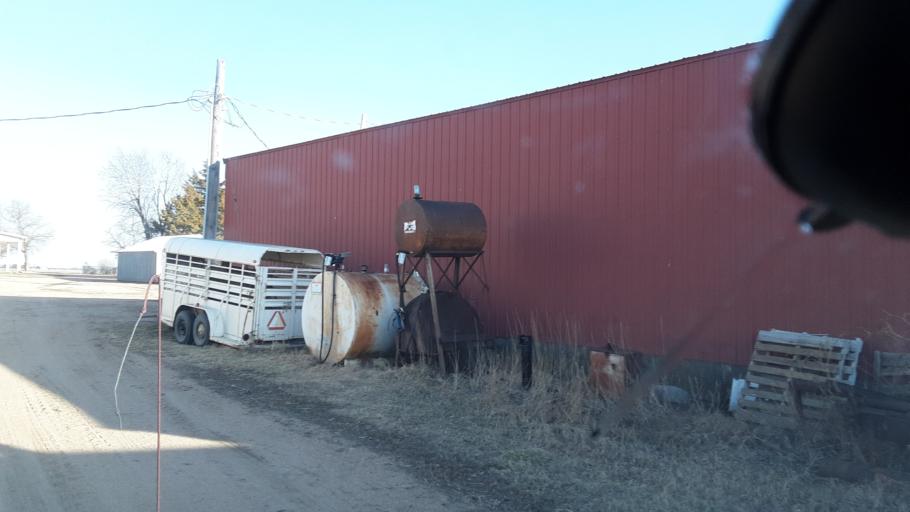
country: US
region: Kansas
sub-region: Reno County
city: South Hutchinson
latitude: 37.9928
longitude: -97.9972
